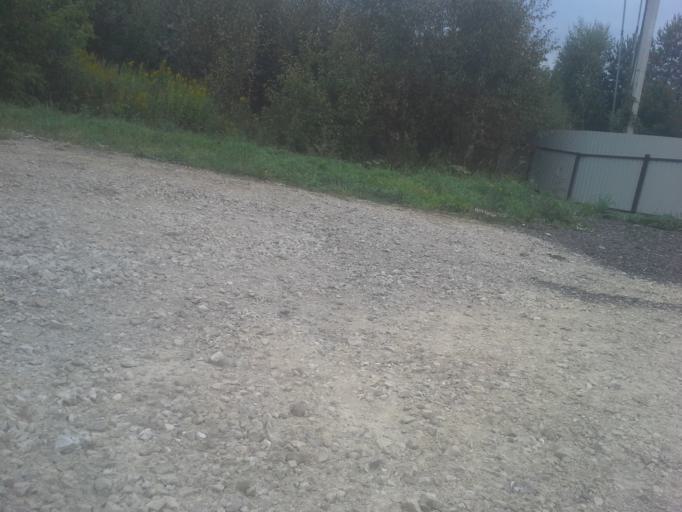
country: RU
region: Moskovskaya
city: Kievskij
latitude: 55.3512
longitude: 36.9068
